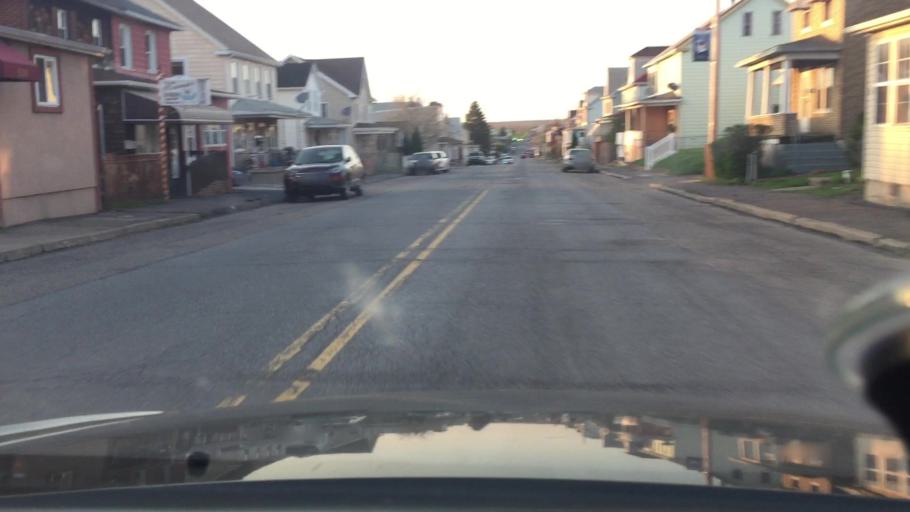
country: US
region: Pennsylvania
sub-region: Schuylkill County
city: McAdoo
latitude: 40.8960
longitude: -75.9948
